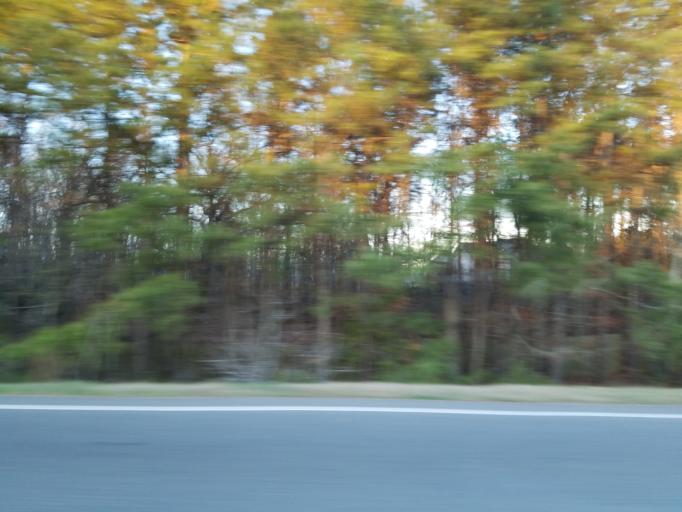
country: US
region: Georgia
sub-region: Hall County
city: Oakwood
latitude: 34.3181
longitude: -84.0018
